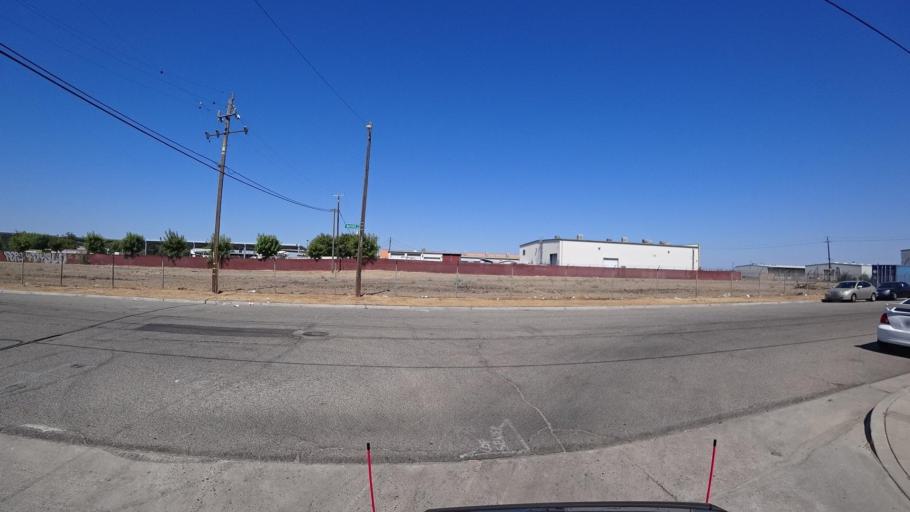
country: US
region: California
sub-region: Fresno County
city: Fresno
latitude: 36.7568
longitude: -119.7431
